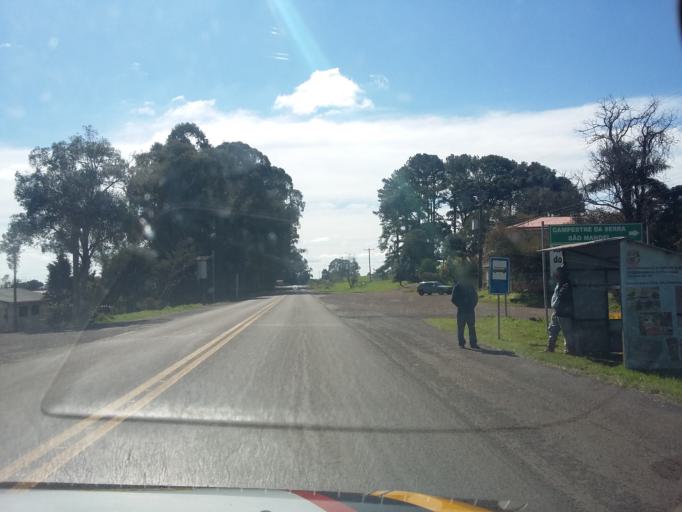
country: BR
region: Rio Grande do Sul
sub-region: Sao Marcos
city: Sao Marcos
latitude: -28.7199
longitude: -51.0873
